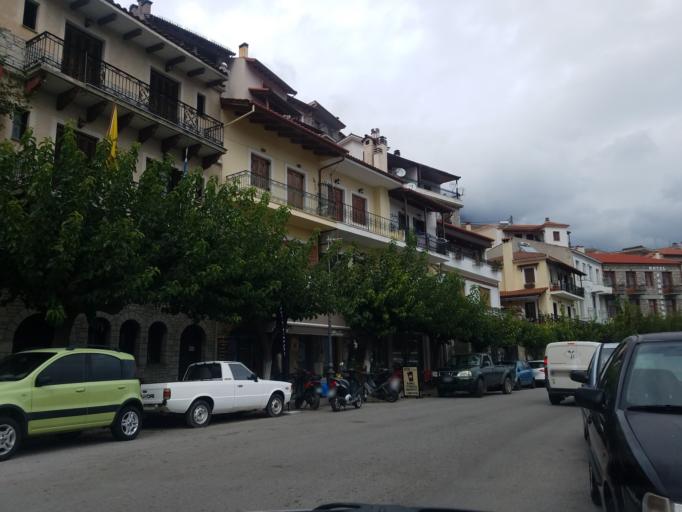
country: GR
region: Central Greece
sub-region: Nomos Voiotias
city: Arachova
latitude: 38.4810
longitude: 22.5863
